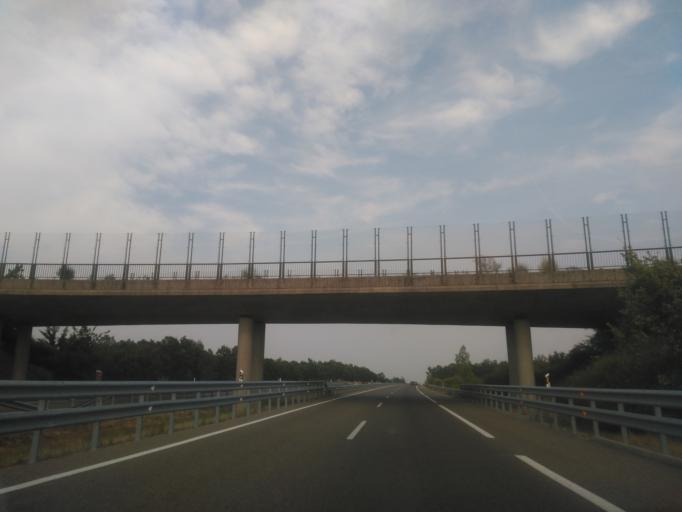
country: ES
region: Castille and Leon
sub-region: Provincia de Zamora
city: Manzanal de los Infantes
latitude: 42.0225
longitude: -6.3711
